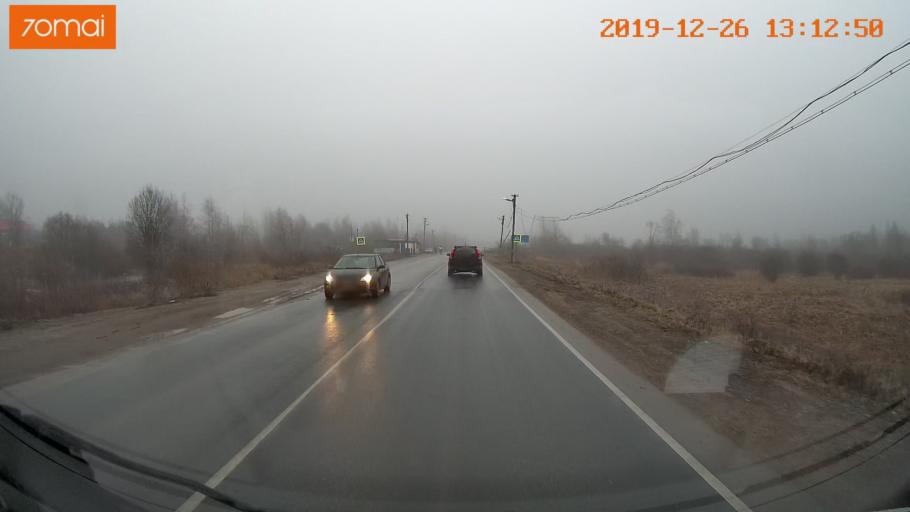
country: RU
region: Vologda
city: Cherepovets
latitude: 59.0213
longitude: 38.0420
